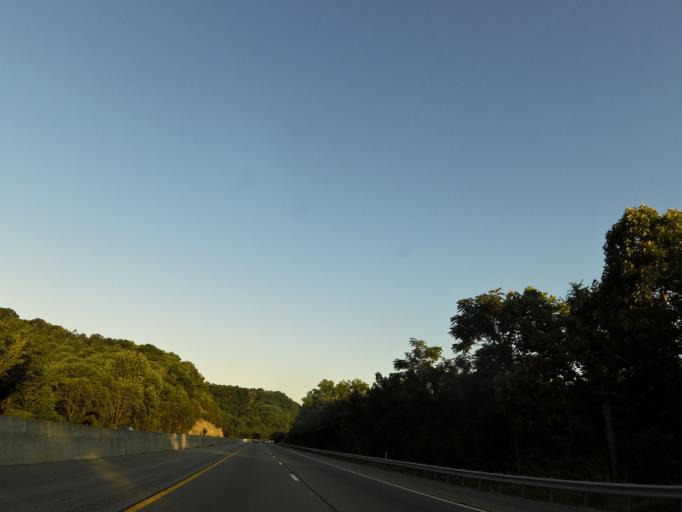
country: US
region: Tennessee
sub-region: Putnam County
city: Lafayette
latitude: 36.1162
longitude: -85.7756
